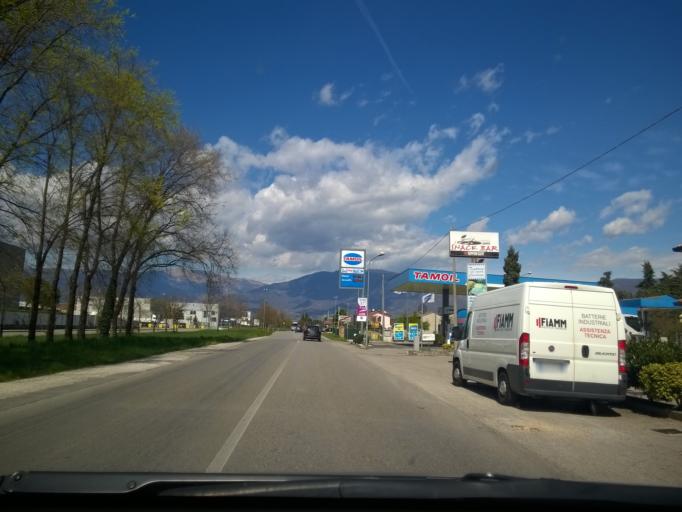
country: IT
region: Veneto
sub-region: Provincia di Treviso
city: San Fior di Sopra
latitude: 45.9298
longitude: 12.3761
